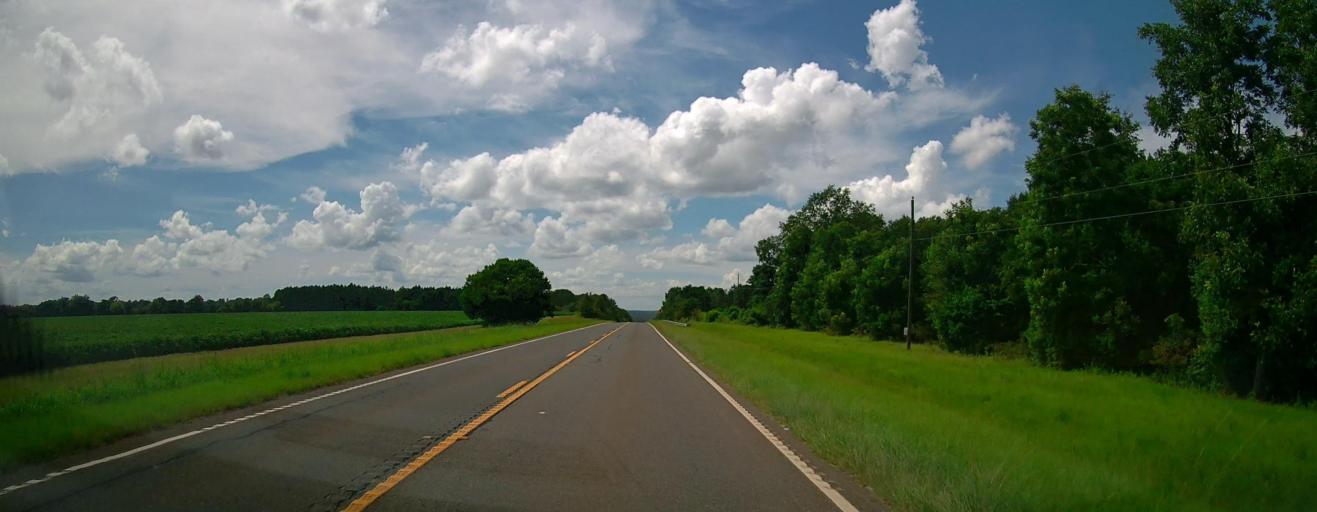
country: US
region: Georgia
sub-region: Macon County
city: Marshallville
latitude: 32.4325
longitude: -84.0096
